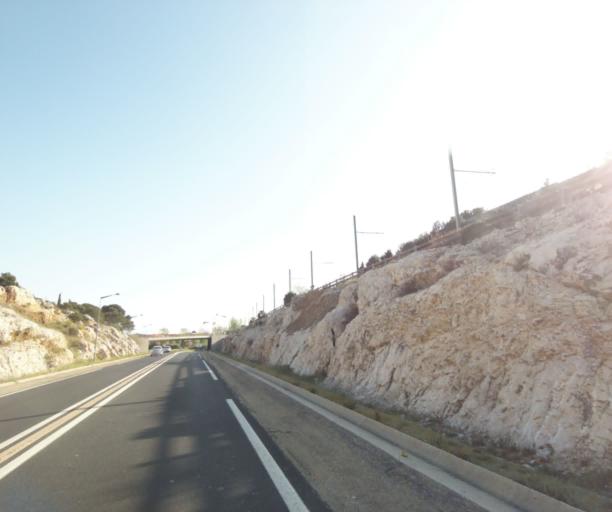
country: FR
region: Languedoc-Roussillon
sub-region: Departement de l'Herault
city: Le Cres
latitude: 43.6419
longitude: 3.9309
